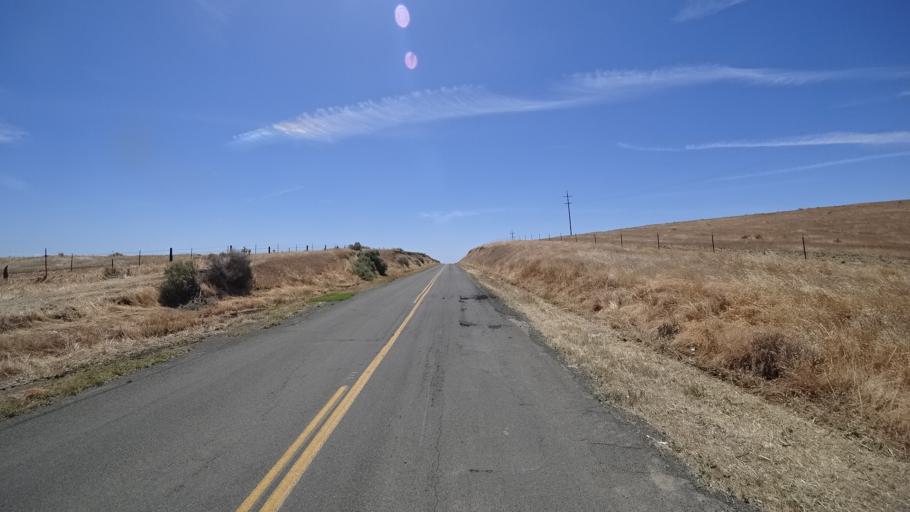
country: US
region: California
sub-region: Kings County
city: Kettleman City
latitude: 35.8967
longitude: -119.9151
